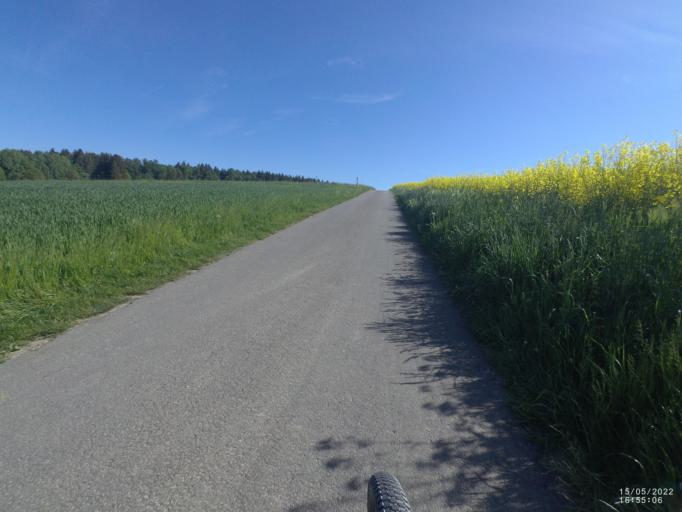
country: DE
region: Baden-Wuerttemberg
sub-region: Regierungsbezirk Stuttgart
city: Bolheim
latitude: 48.5940
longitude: 10.1420
